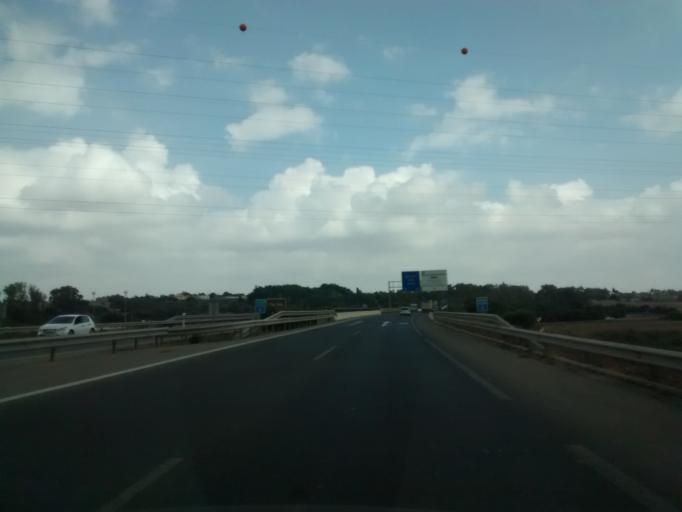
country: ES
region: Andalusia
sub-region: Provincia de Cadiz
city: Chiclana de la Frontera
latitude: 36.4149
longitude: -6.1186
